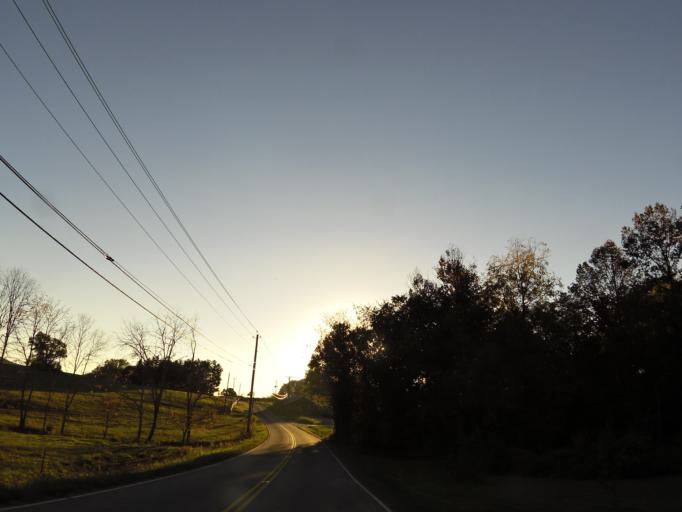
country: US
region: Tennessee
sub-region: Grainger County
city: Rutledge
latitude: 36.2844
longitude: -83.6110
